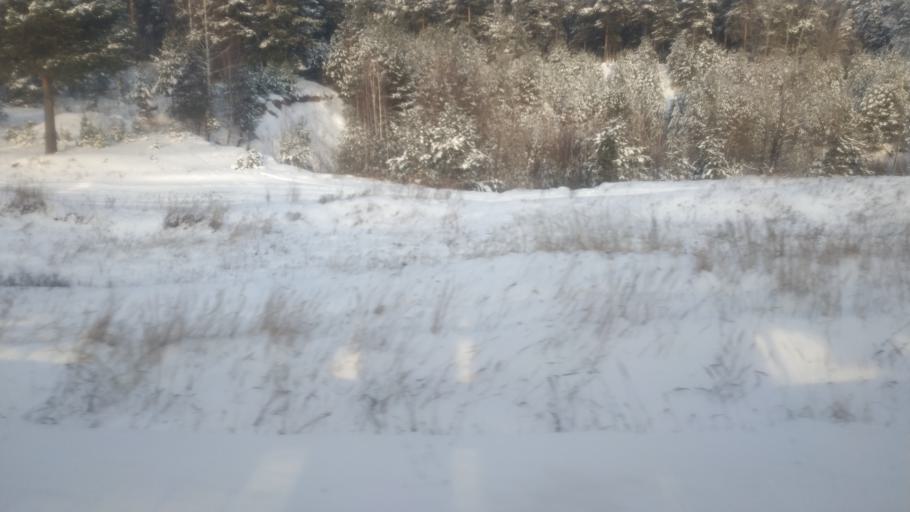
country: RU
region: Kirov
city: Krasnaya Polyana
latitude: 56.2477
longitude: 51.1603
